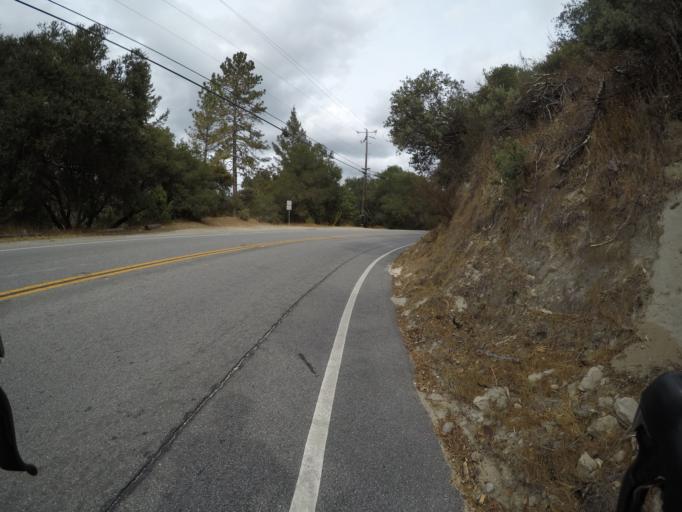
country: US
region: California
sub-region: Santa Cruz County
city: Ben Lomond
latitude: 37.0824
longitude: -122.0760
